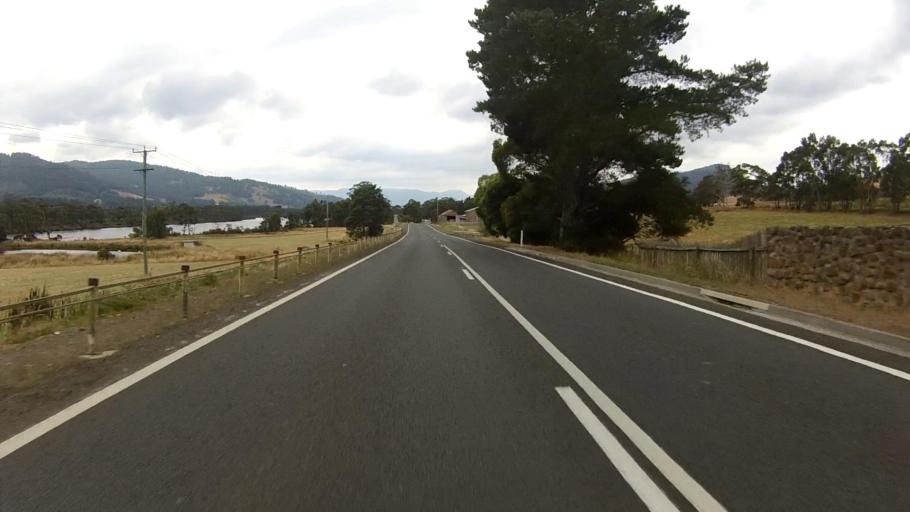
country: AU
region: Tasmania
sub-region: Huon Valley
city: Franklin
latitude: -43.0847
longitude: 147.0300
